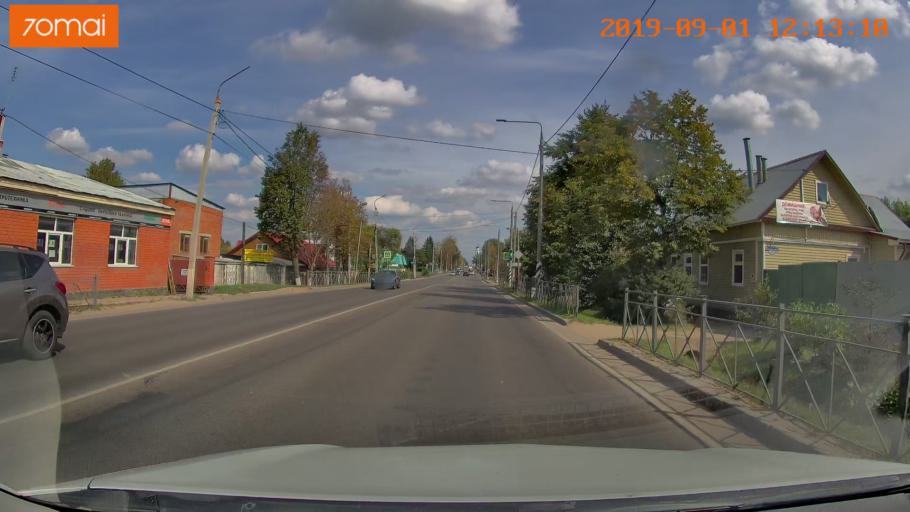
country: RU
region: Kaluga
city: Maloyaroslavets
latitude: 55.0072
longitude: 36.4500
